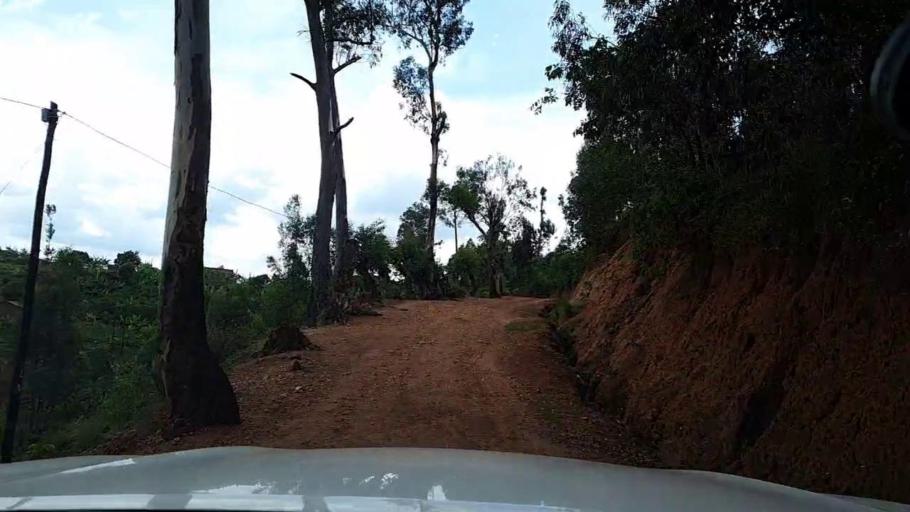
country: RW
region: Southern Province
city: Butare
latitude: -2.7533
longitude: 29.7541
